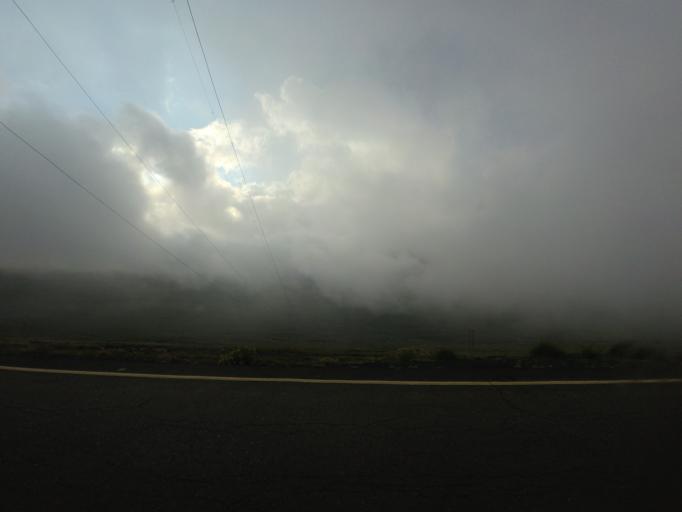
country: LS
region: Butha-Buthe
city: Butha-Buthe
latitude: -29.0667
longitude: 28.4136
